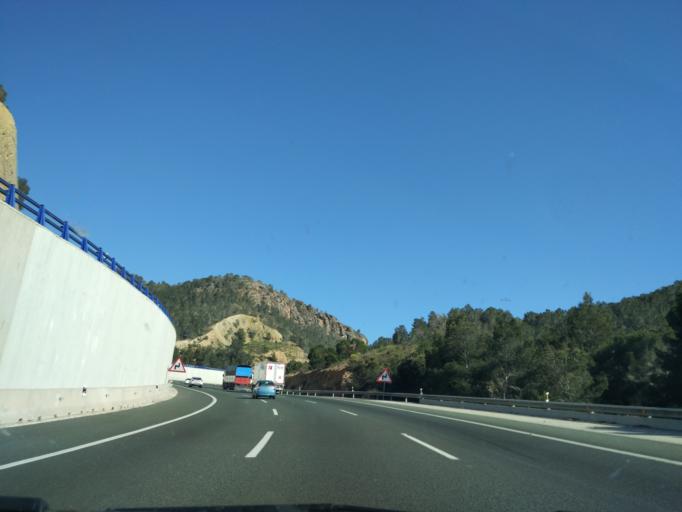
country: ES
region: Murcia
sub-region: Murcia
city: Murcia
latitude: 37.9061
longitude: -1.1496
